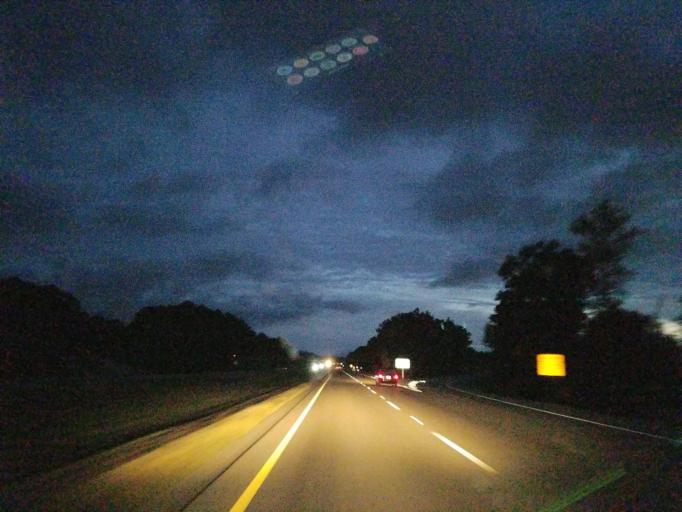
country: US
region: Mississippi
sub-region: Jones County
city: Sharon
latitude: 31.7877
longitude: -89.0552
